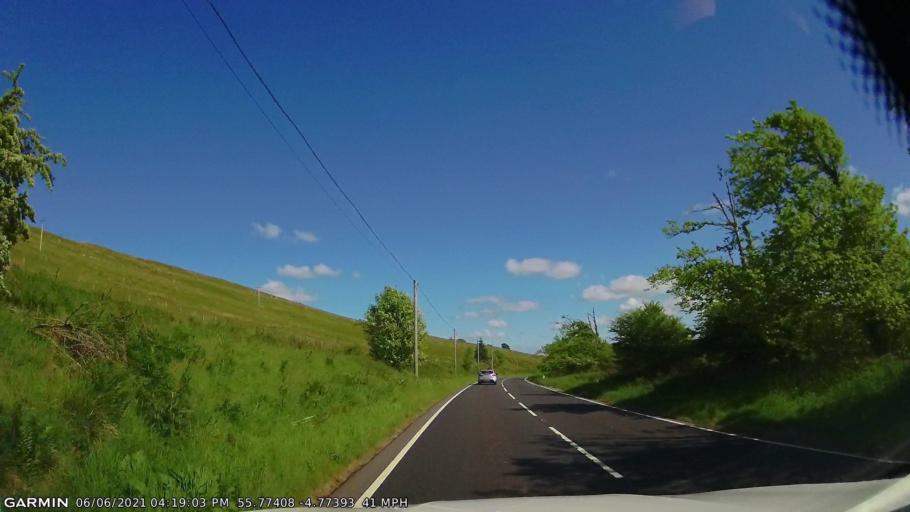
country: GB
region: Scotland
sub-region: North Ayrshire
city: Dalry
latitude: 55.7741
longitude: -4.7739
